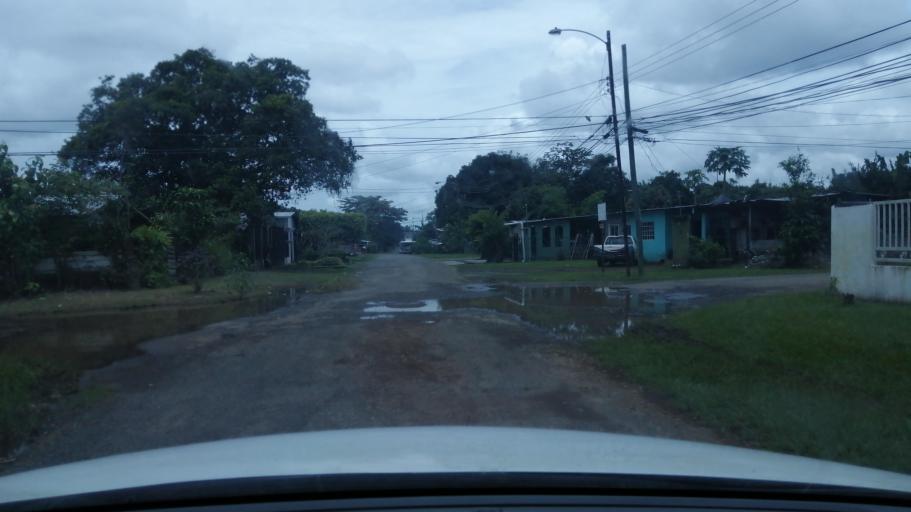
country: PA
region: Chiriqui
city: David
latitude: 8.4183
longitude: -82.4428
